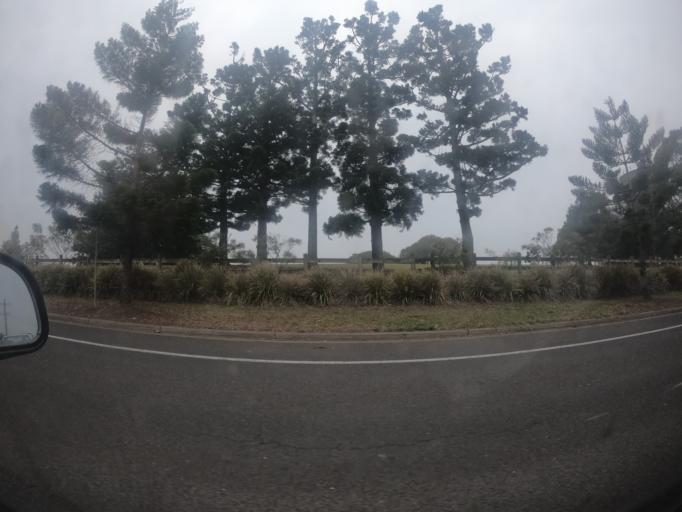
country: AU
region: New South Wales
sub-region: Shellharbour
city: Croom
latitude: -34.5729
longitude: 150.8318
